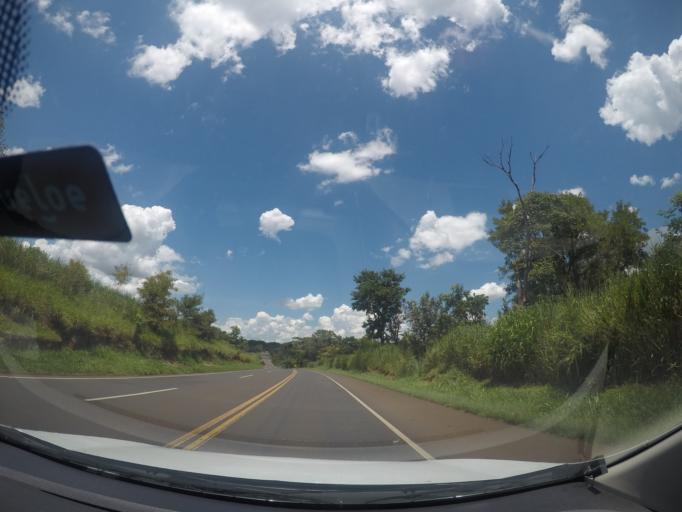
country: BR
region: Minas Gerais
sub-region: Monte Alegre De Minas
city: Monte Alegre de Minas
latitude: -19.0362
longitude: -49.0119
